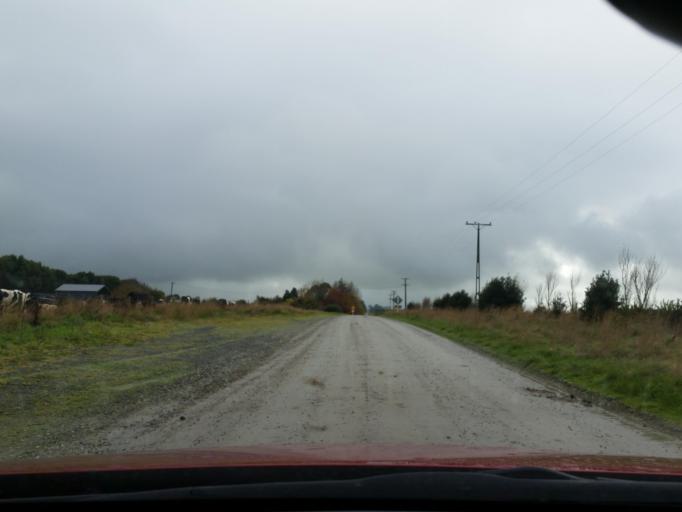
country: NZ
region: Southland
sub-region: Invercargill City
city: Invercargill
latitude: -46.3133
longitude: 168.5565
